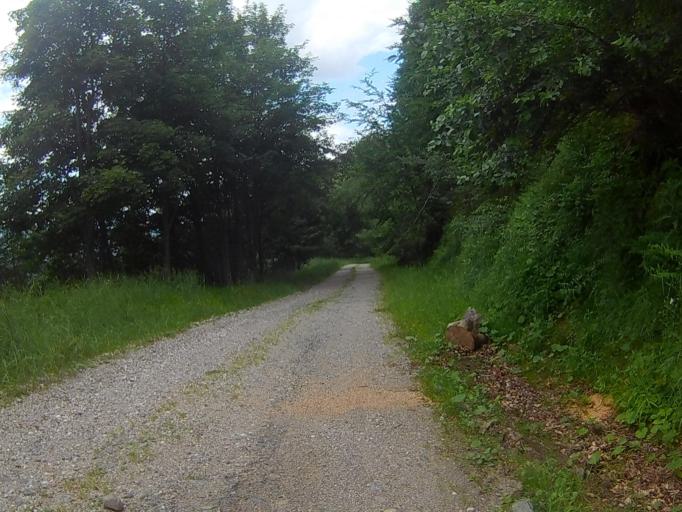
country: SI
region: Selnica ob Dravi
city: Selnica ob Dravi
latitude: 46.5078
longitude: 15.4653
